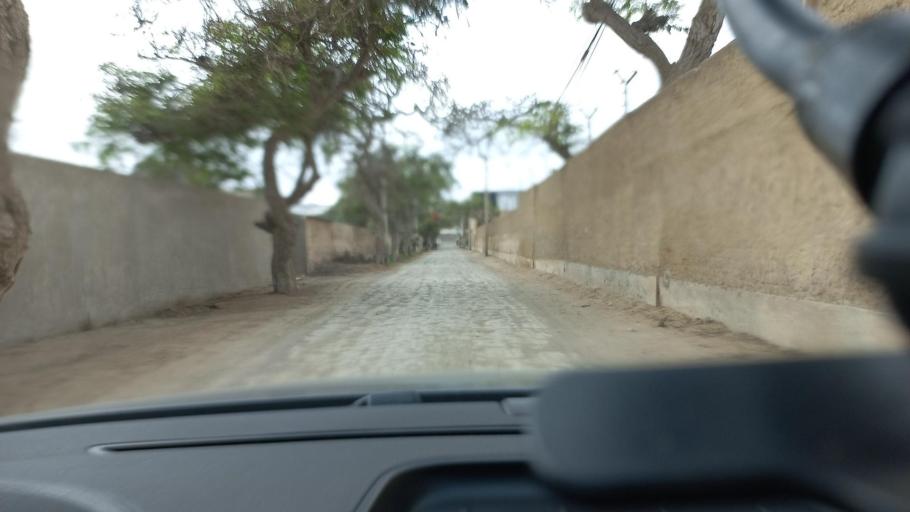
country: PE
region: Lima
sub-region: Lima
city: Punta Hermosa
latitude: -12.2566
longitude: -76.9125
